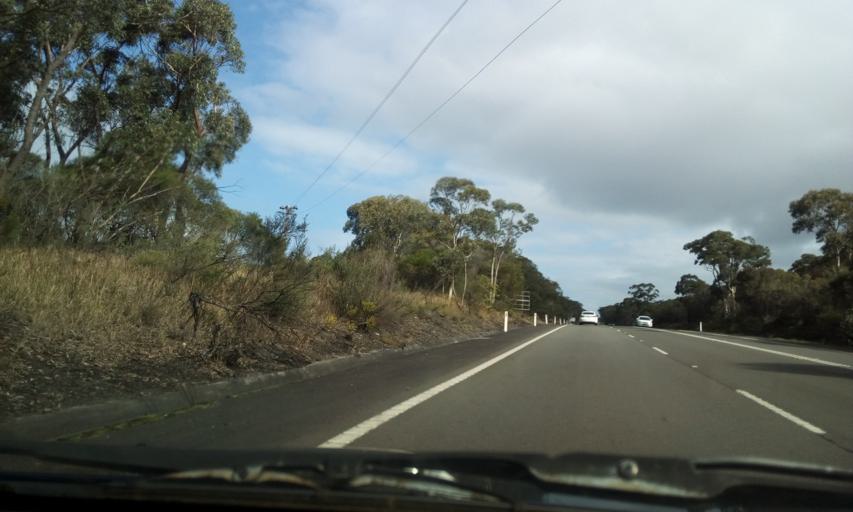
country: AU
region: New South Wales
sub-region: Wollongong
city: Bulli
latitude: -34.2875
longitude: 150.9013
